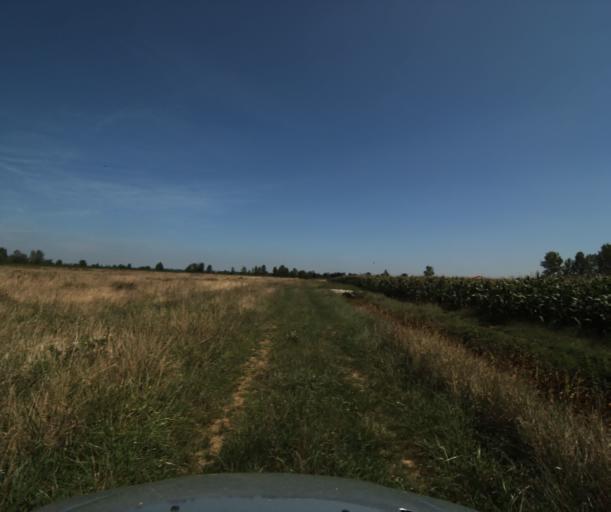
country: FR
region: Midi-Pyrenees
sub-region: Departement de la Haute-Garonne
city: Labastidette
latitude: 43.4711
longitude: 1.2647
